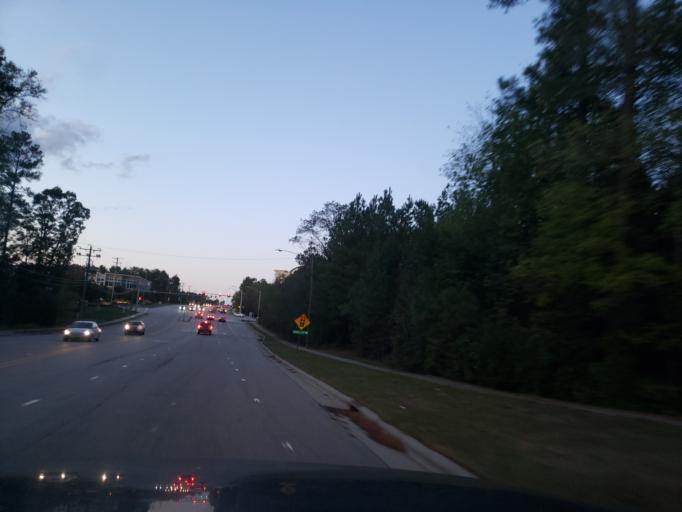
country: US
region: North Carolina
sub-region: Orange County
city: Chapel Hill
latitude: 35.8994
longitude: -78.9593
